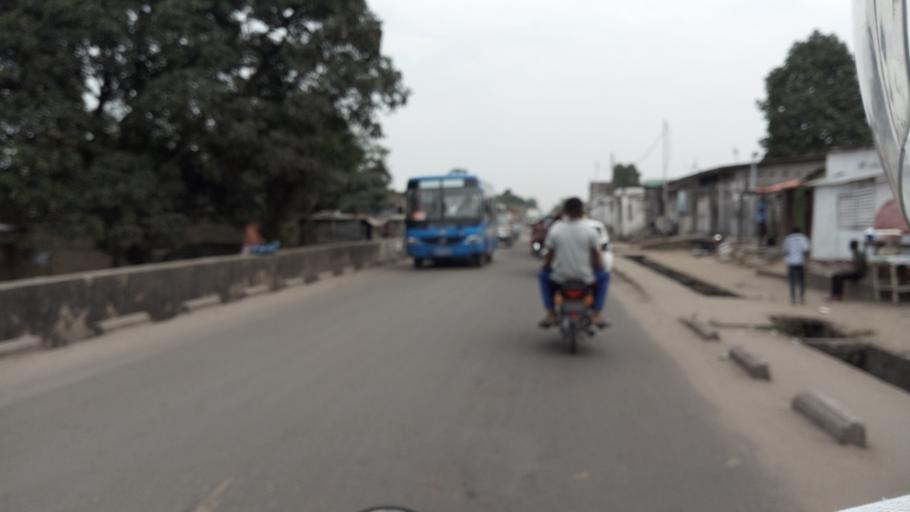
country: CD
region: Kinshasa
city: Masina
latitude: -4.4076
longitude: 15.3163
